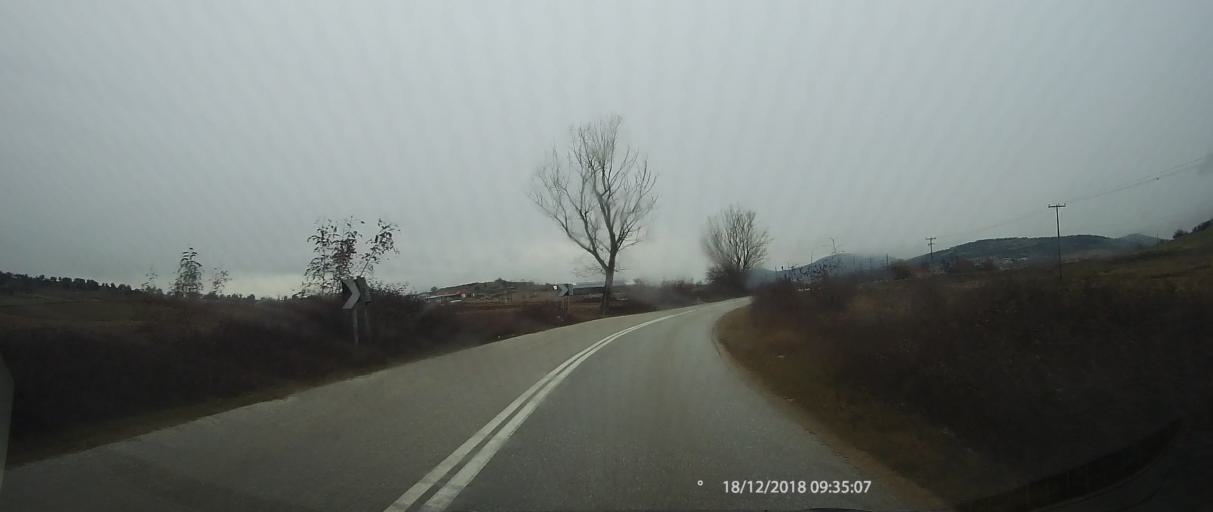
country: GR
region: Thessaly
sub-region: Nomos Larisis
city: Elassona
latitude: 39.9814
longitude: 22.1846
